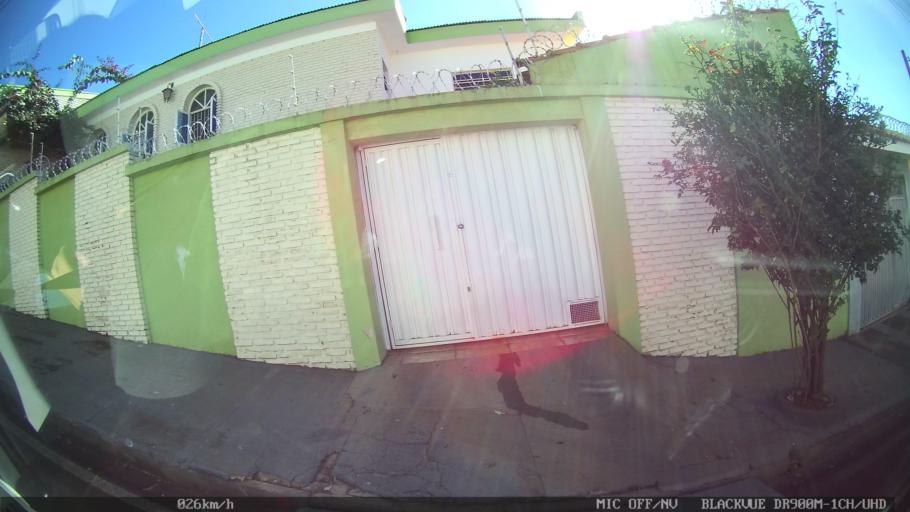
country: BR
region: Sao Paulo
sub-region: Franca
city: Franca
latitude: -20.5388
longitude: -47.4086
